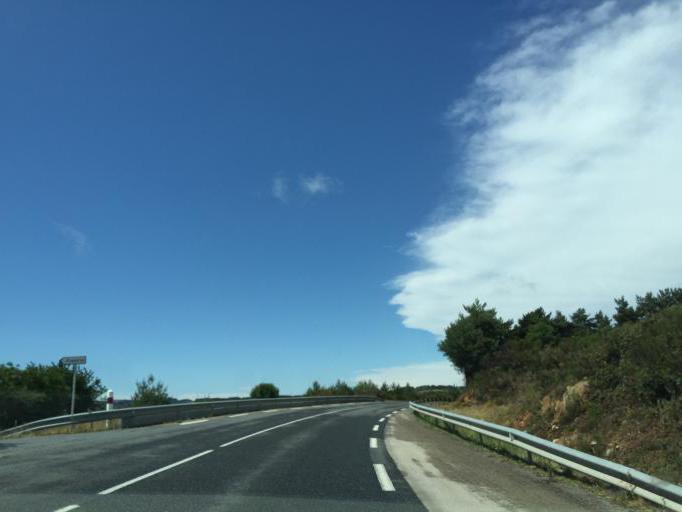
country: FR
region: Midi-Pyrenees
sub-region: Departement de l'Aveyron
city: Severac-le-Chateau
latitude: 44.2260
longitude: 2.9888
